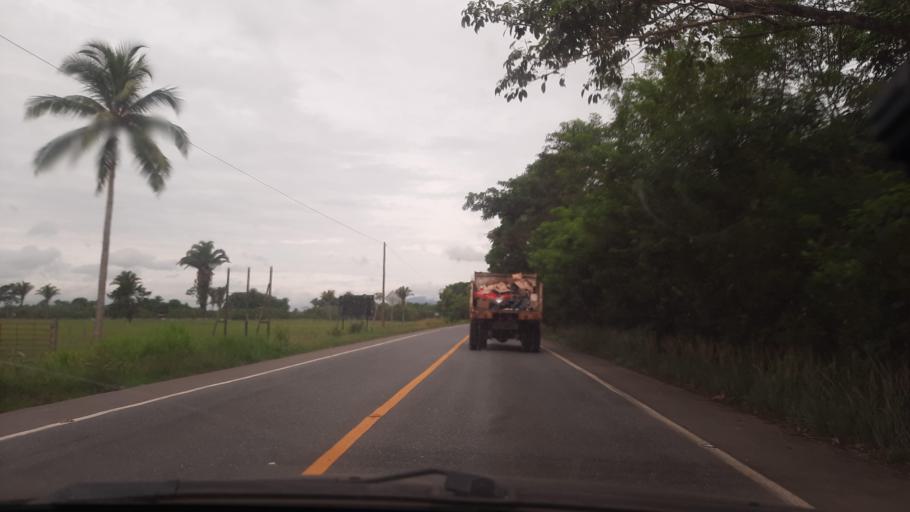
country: GT
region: Izabal
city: Morales
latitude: 15.4702
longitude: -88.9034
